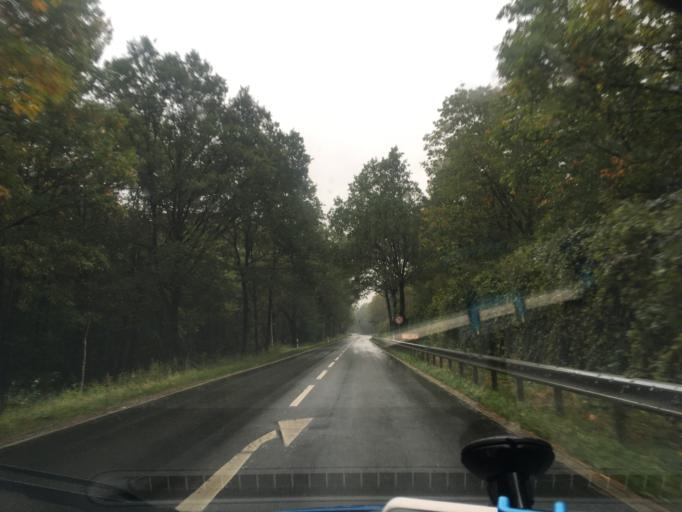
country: DE
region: Lower Saxony
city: Bispingen
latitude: 53.0642
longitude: 9.9945
